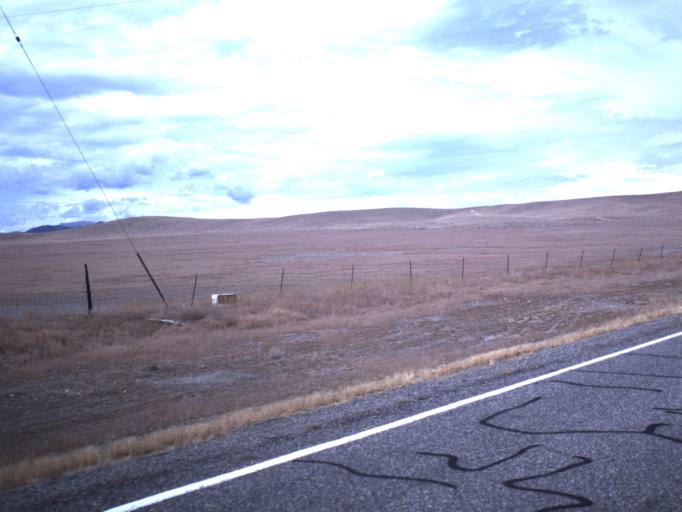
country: US
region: Utah
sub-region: Sevier County
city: Monroe
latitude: 38.6290
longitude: -112.1620
